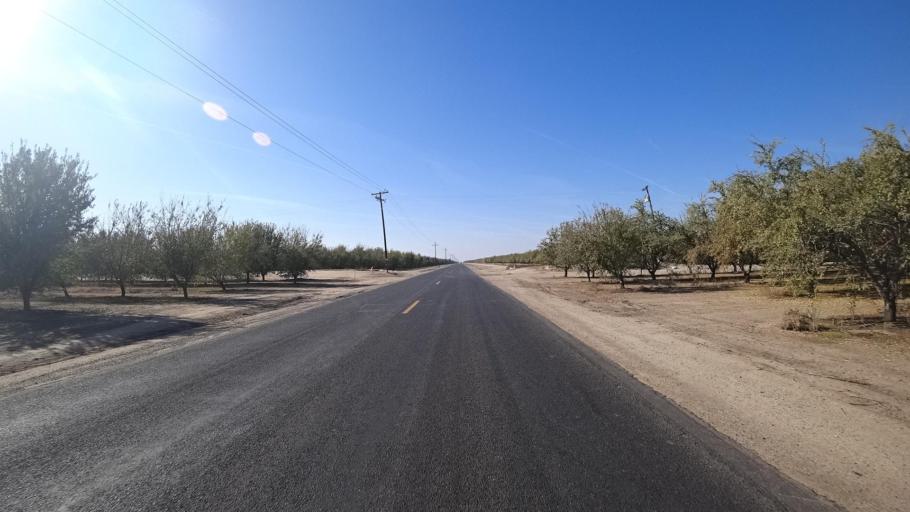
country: US
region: California
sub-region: Kern County
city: McFarland
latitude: 35.6454
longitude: -119.2584
